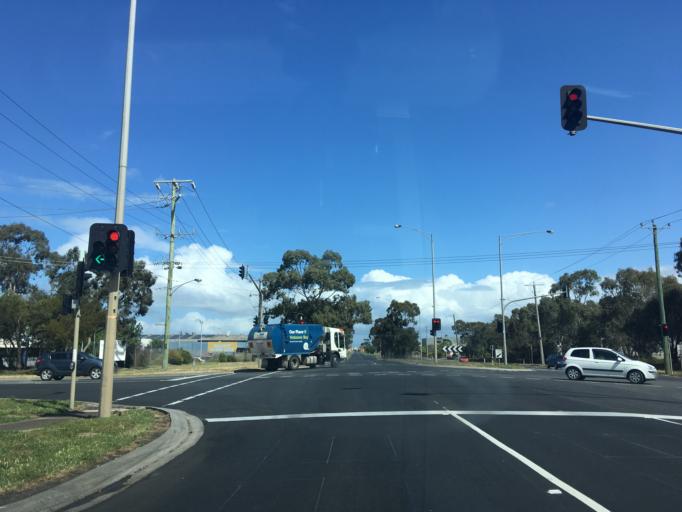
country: AU
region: Victoria
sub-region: Brimbank
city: Derrimut
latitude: -37.8205
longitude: 144.7866
